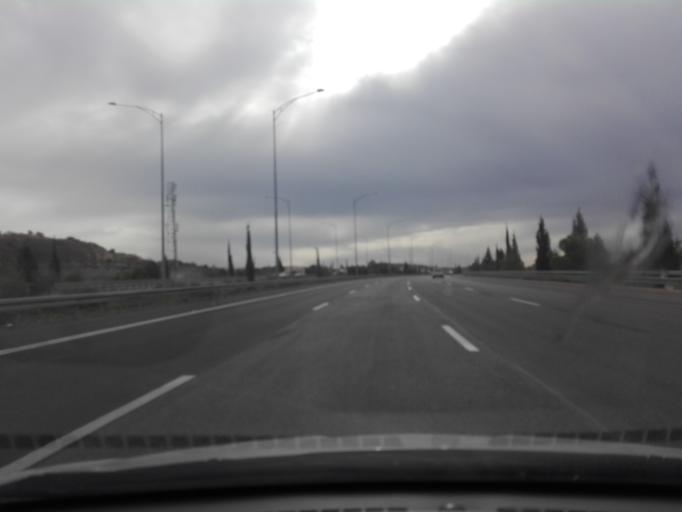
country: PS
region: West Bank
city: Rantis
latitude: 32.0217
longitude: 34.9653
